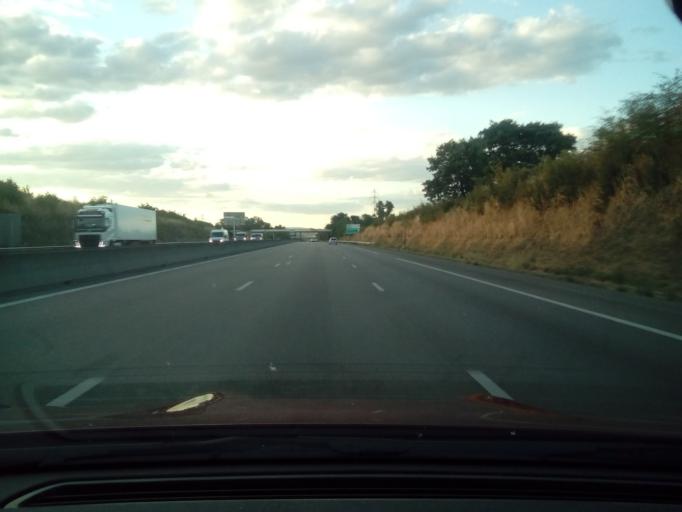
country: FR
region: Rhone-Alpes
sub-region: Departement de l'Isere
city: Salaise-sur-Sanne
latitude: 45.3333
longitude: 4.8108
